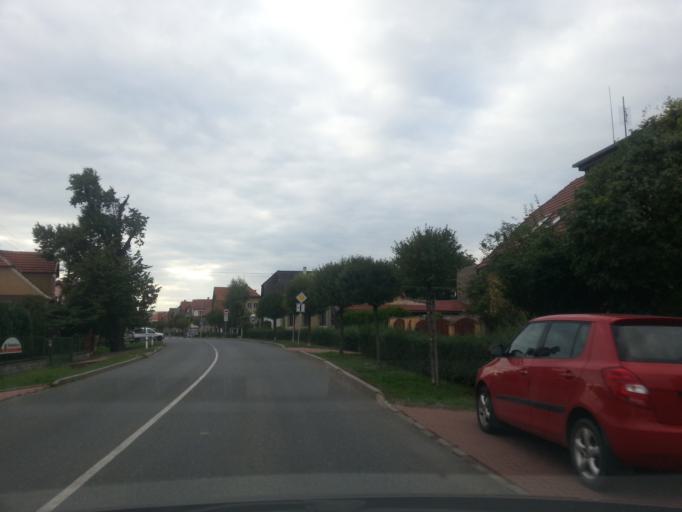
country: CZ
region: Central Bohemia
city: Unhost'
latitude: 50.0858
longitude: 14.1400
